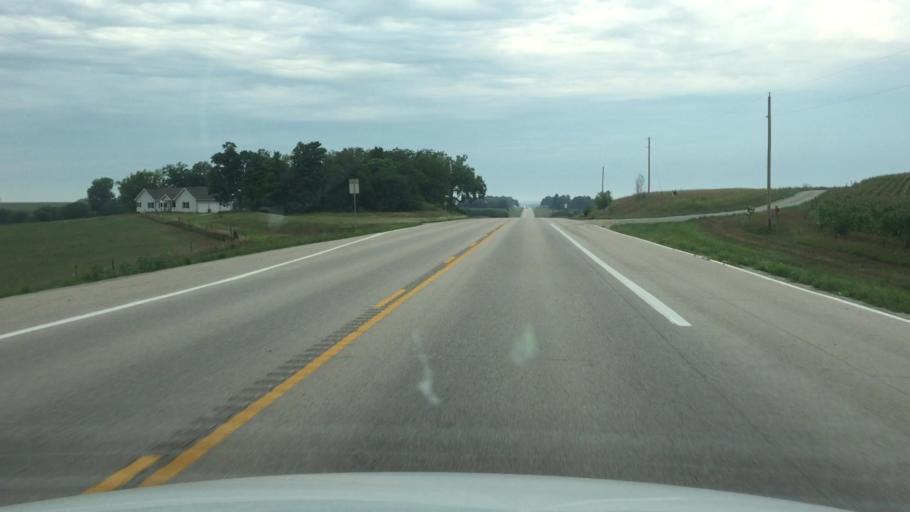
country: US
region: Kansas
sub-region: Brown County
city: Hiawatha
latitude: 39.8486
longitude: -95.5995
